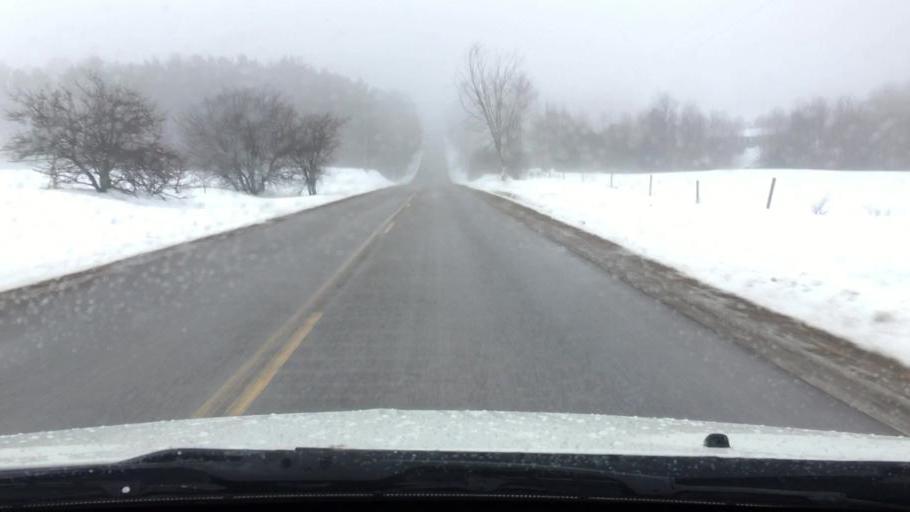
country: US
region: Michigan
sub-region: Charlevoix County
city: East Jordan
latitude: 45.1294
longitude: -85.1802
